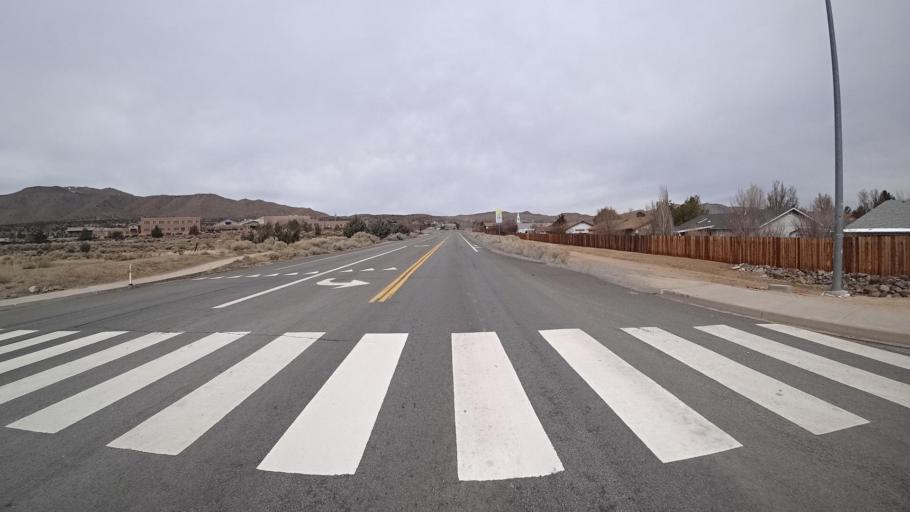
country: US
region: Nevada
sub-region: Washoe County
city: Spanish Springs
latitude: 39.6488
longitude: -119.7258
